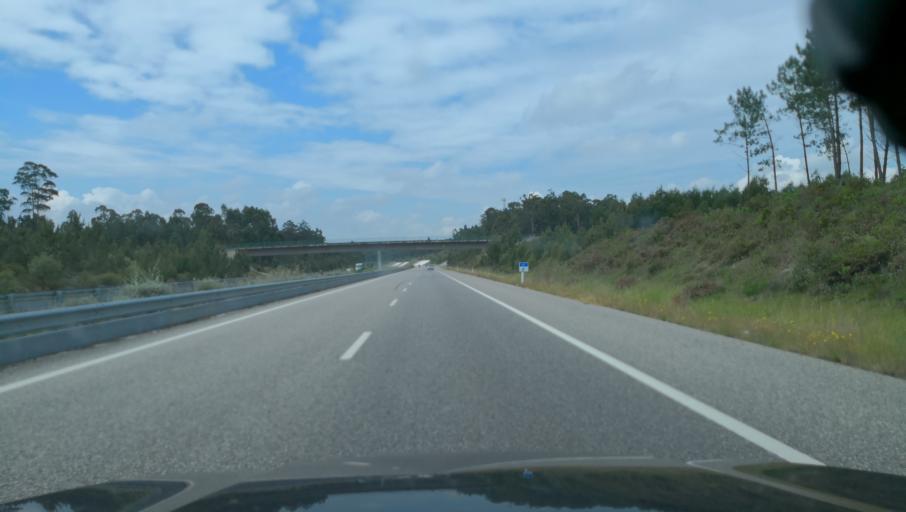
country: PT
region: Leiria
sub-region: Leiria
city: Amor
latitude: 39.7907
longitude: -8.8614
